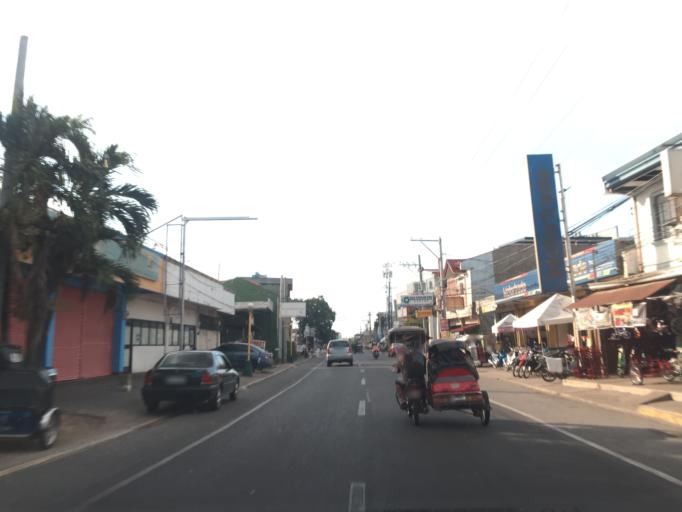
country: PH
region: Ilocos
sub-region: Province of Pangasinan
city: Bolingit
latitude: 15.9316
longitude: 120.3480
